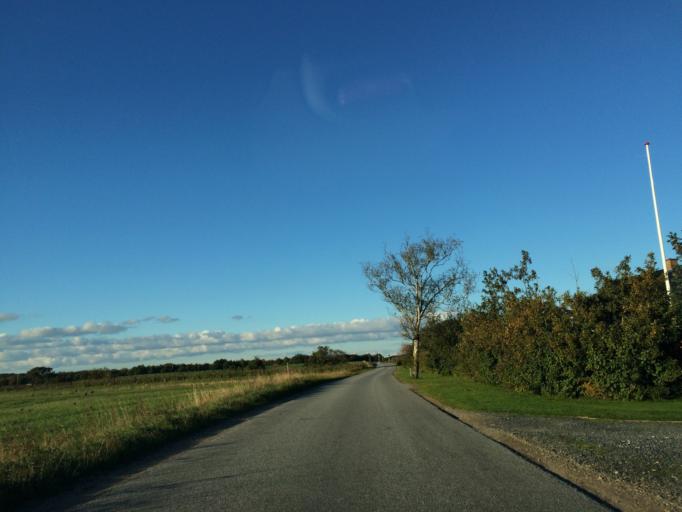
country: DK
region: Central Jutland
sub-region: Silkeborg Kommune
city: Svejbaek
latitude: 56.1807
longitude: 9.6920
